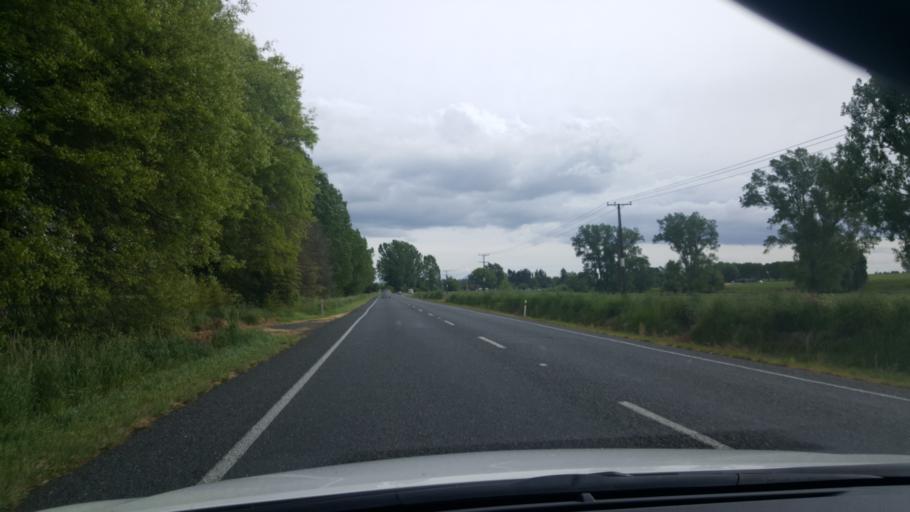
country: NZ
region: Waikato
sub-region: Taupo District
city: Taupo
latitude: -38.4611
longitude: 176.3156
